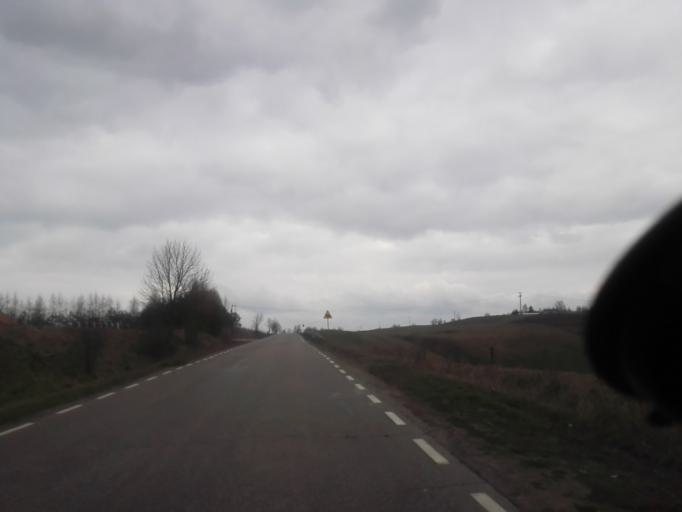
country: PL
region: Podlasie
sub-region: Suwalki
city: Suwalki
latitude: 54.2263
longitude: 22.9120
